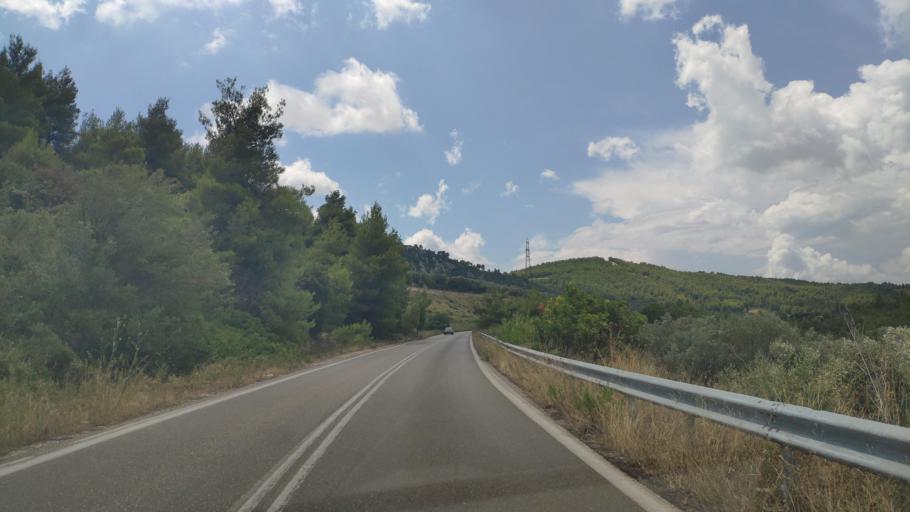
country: GR
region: Central Greece
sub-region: Nomos Fthiotidos
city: Martinon
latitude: 38.6052
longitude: 23.1783
